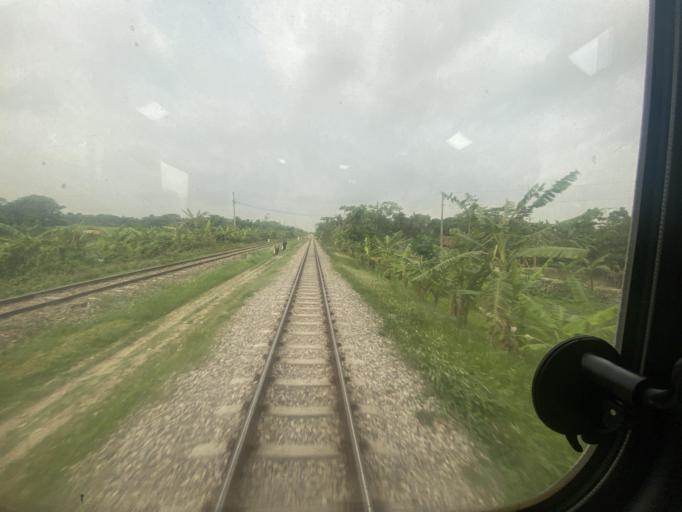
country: BD
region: Dhaka
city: Tungi
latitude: 23.9307
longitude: 90.5344
